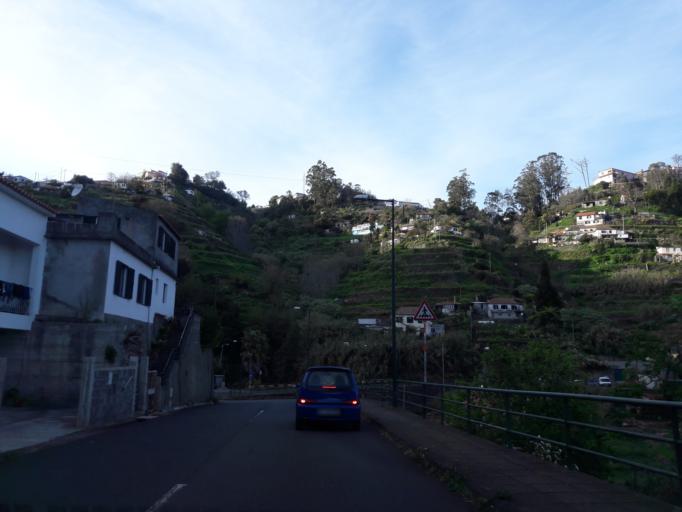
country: PT
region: Madeira
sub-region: Santa Cruz
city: Camacha
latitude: 32.6662
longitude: -16.8496
